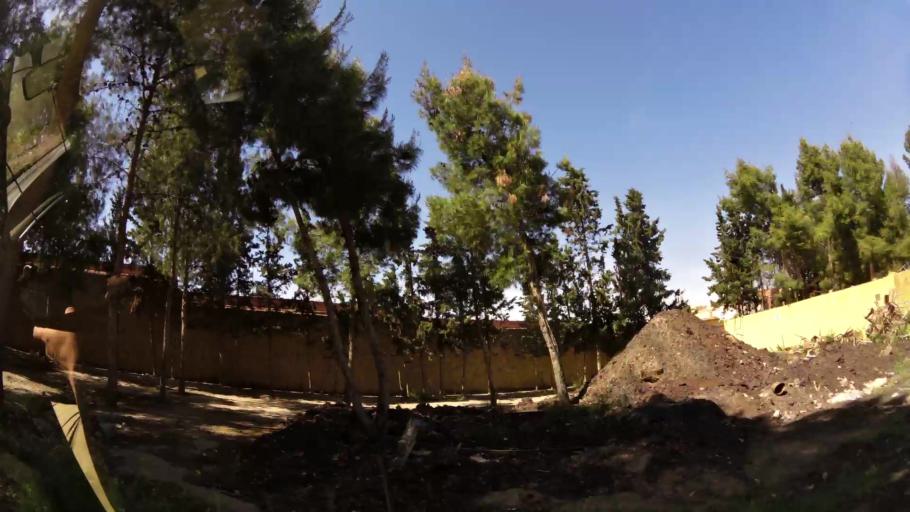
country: MA
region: Oriental
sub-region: Oujda-Angad
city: Oujda
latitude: 34.6518
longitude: -1.9081
